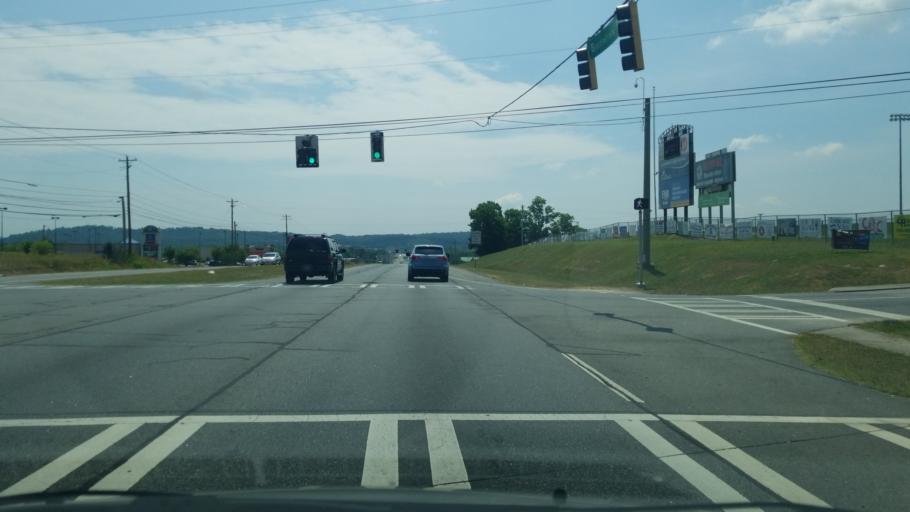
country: US
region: Georgia
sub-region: Catoosa County
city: Fort Oglethorpe
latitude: 34.9477
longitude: -85.2339
